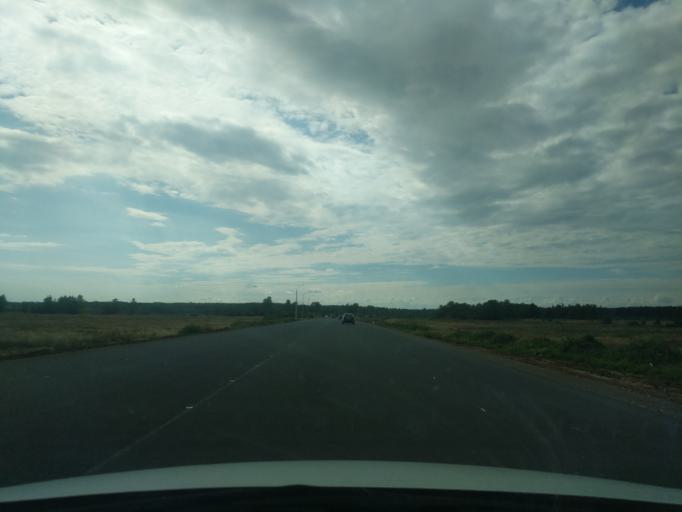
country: RU
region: Kostroma
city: Sudislavl'
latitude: 57.8305
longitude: 41.5424
